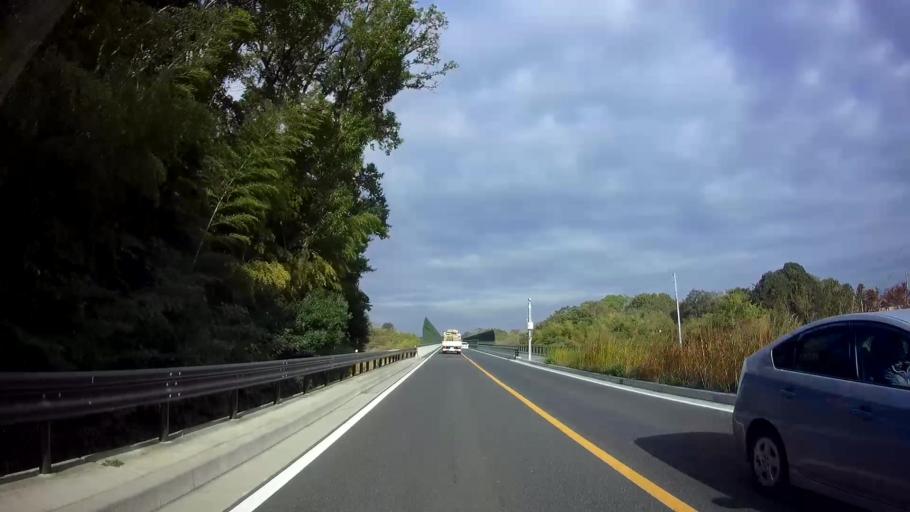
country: JP
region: Saitama
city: Okegawa
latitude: 35.9742
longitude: 139.5419
